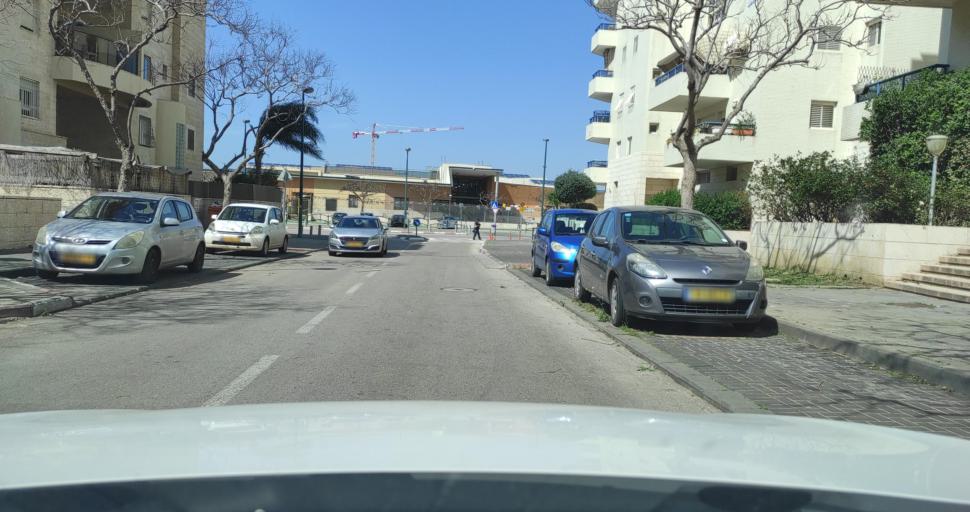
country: IL
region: Central District
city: Bet Yizhaq
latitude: 32.3099
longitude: 34.8716
